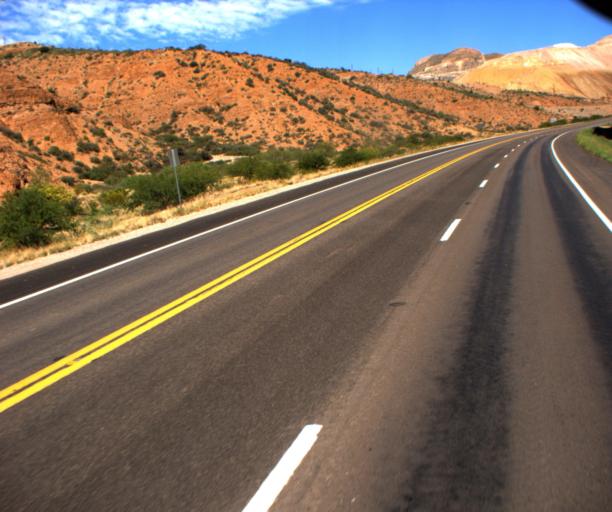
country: US
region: Arizona
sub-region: Greenlee County
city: Clifton
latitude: 33.0600
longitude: -109.3208
